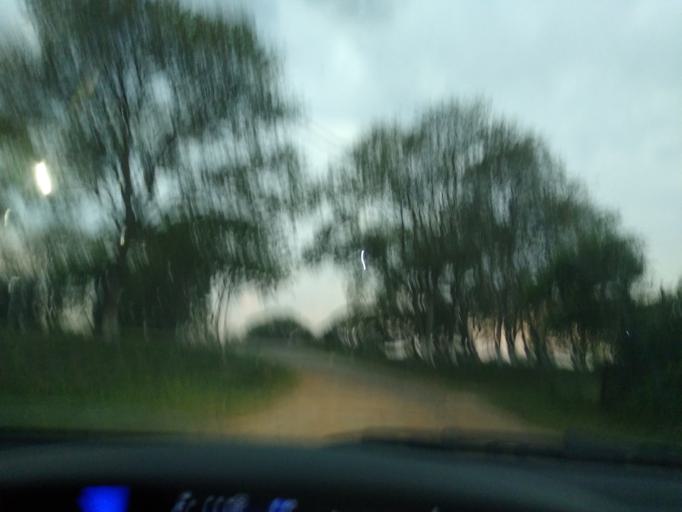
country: AR
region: Chaco
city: Puerto Tirol
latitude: -27.3744
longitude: -59.0822
